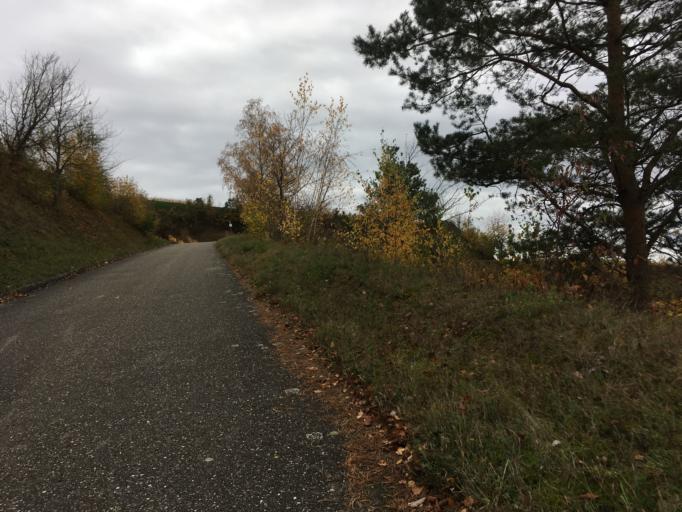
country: DE
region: Baden-Wuerttemberg
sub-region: Freiburg Region
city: Merdingen
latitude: 48.0177
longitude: 7.6973
